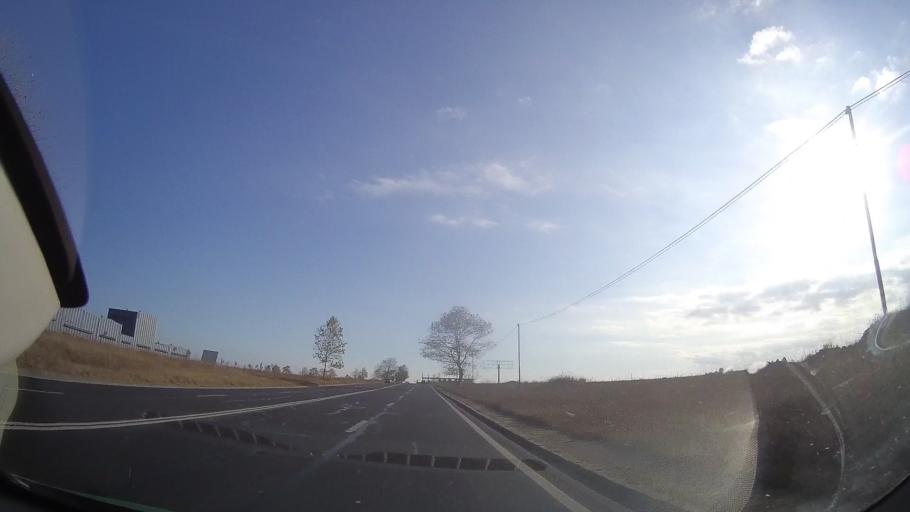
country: RO
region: Constanta
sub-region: Municipiul Mangalia
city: Mangalia
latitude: 43.7973
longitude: 28.5595
